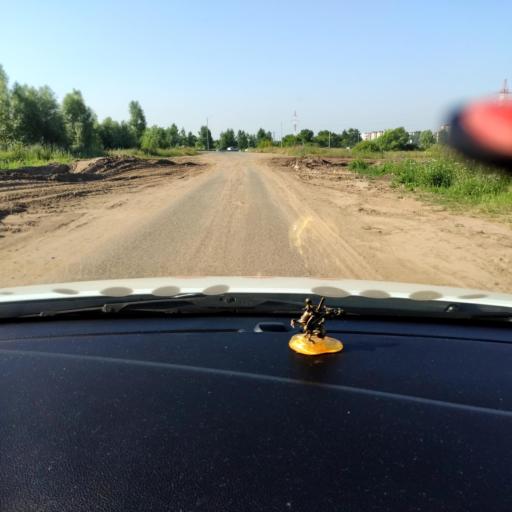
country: RU
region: Tatarstan
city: Stolbishchi
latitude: 55.6964
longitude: 49.2222
